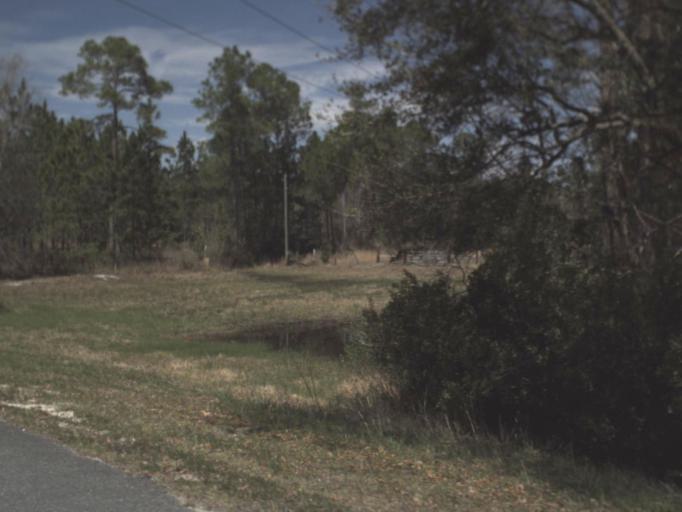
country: US
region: Florida
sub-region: Wakulla County
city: Crawfordville
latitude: 30.2733
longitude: -84.3782
